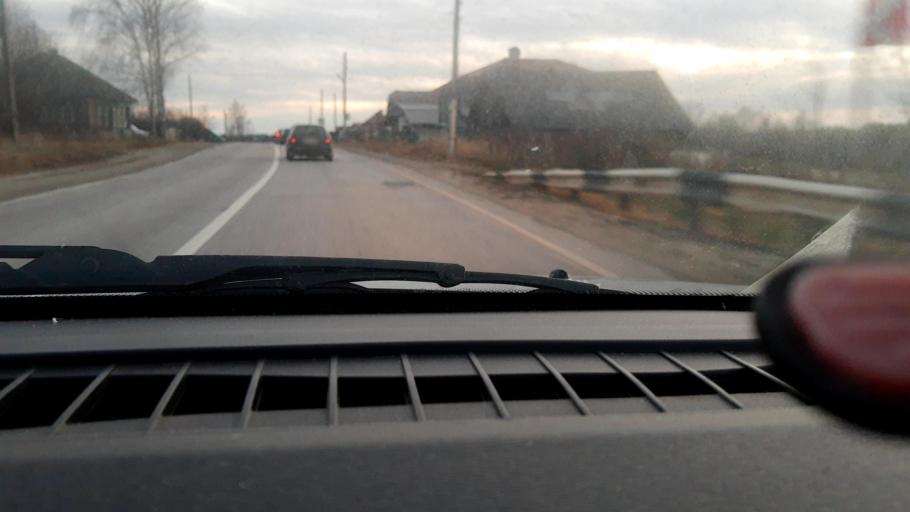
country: RU
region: Nizjnij Novgorod
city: Krasnyye Baki
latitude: 57.0675
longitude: 45.1372
